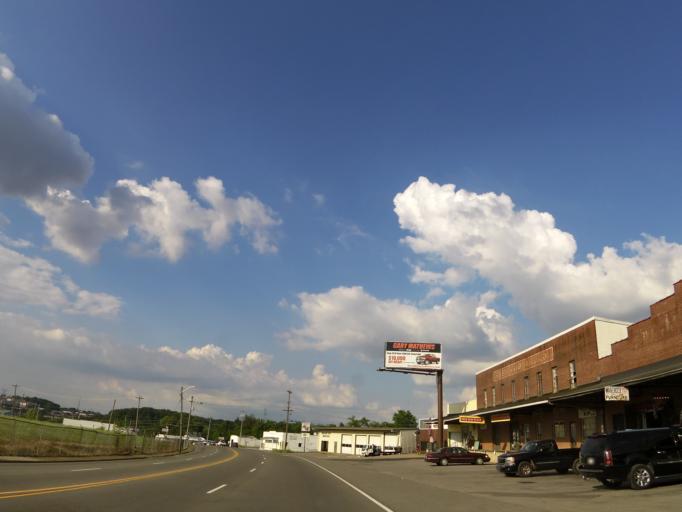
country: US
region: Tennessee
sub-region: Montgomery County
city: Clarksville
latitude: 36.5358
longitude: -87.3397
